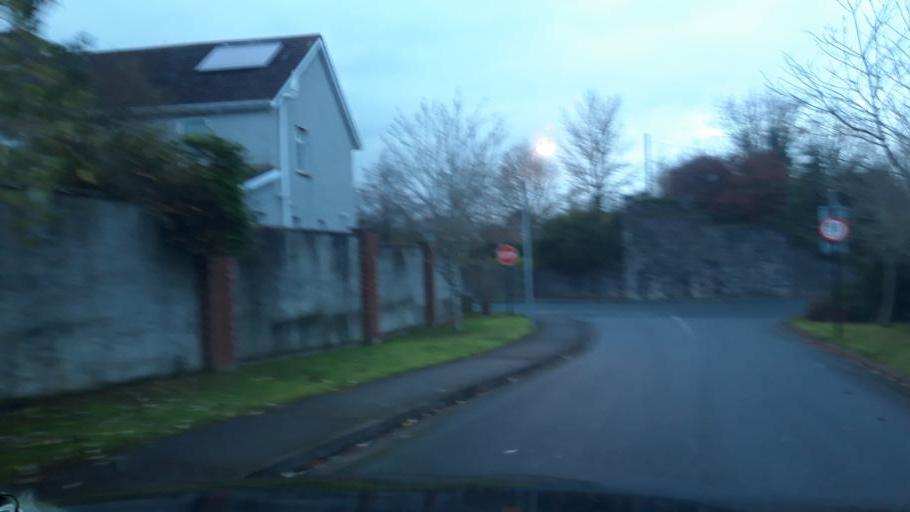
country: IE
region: Leinster
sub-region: Kilkenny
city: Kilkenny
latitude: 52.6585
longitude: -7.2508
